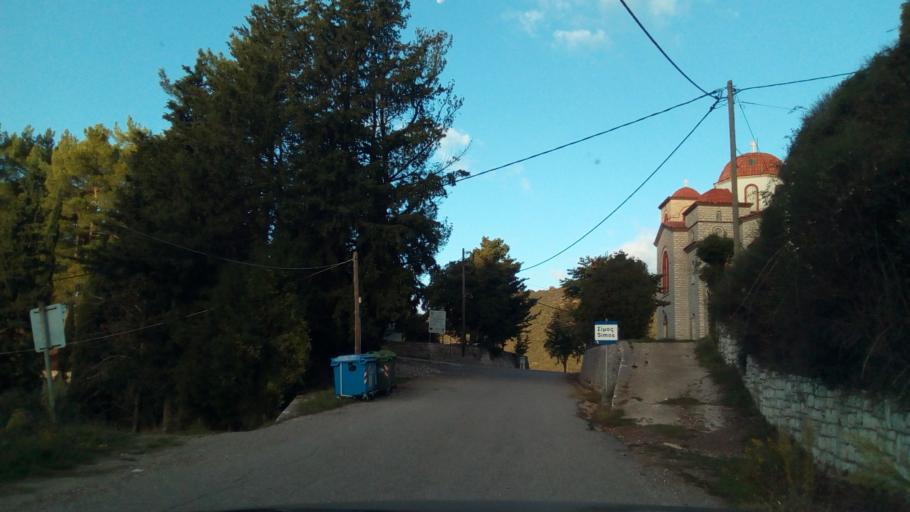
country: GR
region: West Greece
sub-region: Nomos Aitolias kai Akarnanias
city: Nafpaktos
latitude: 38.5327
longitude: 21.8194
